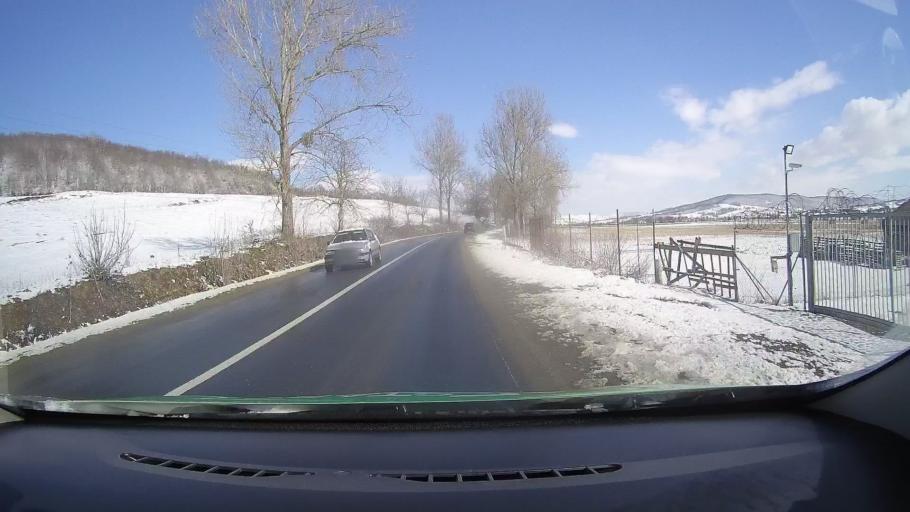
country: RO
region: Sibiu
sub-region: Comuna Nocrich
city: Nocrich
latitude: 45.8351
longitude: 24.4037
